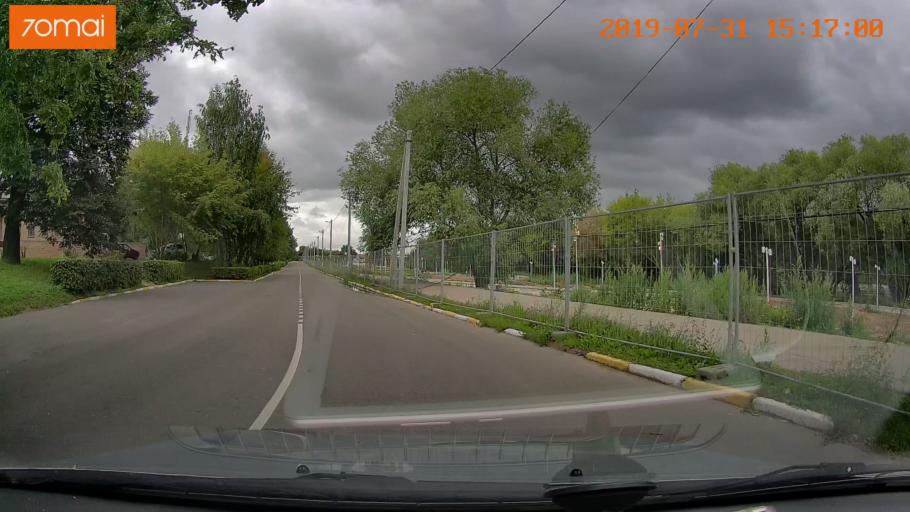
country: RU
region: Moskovskaya
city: Voskresensk
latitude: 55.3186
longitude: 38.6577
